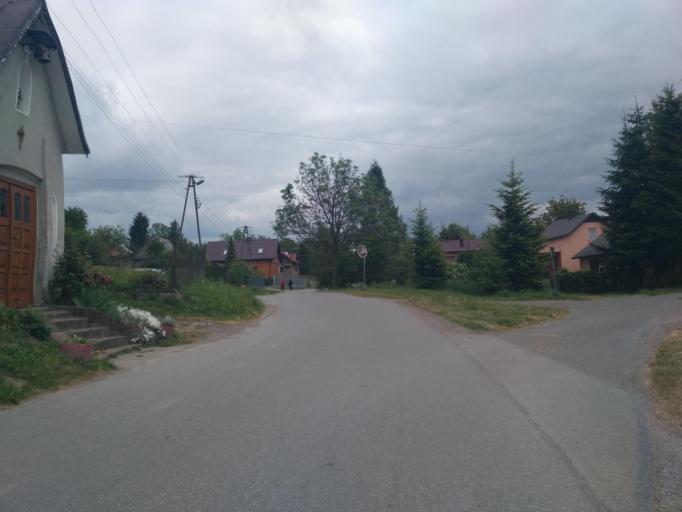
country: PL
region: Subcarpathian Voivodeship
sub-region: Powiat krosnienski
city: Jedlicze
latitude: 49.6884
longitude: 21.6419
